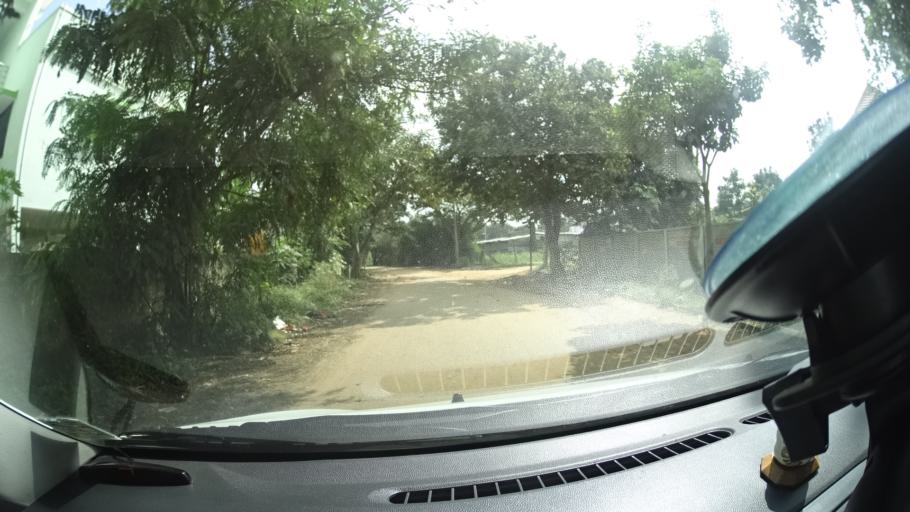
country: IN
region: Karnataka
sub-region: Bangalore Urban
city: Yelahanka
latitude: 13.1010
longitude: 77.5855
